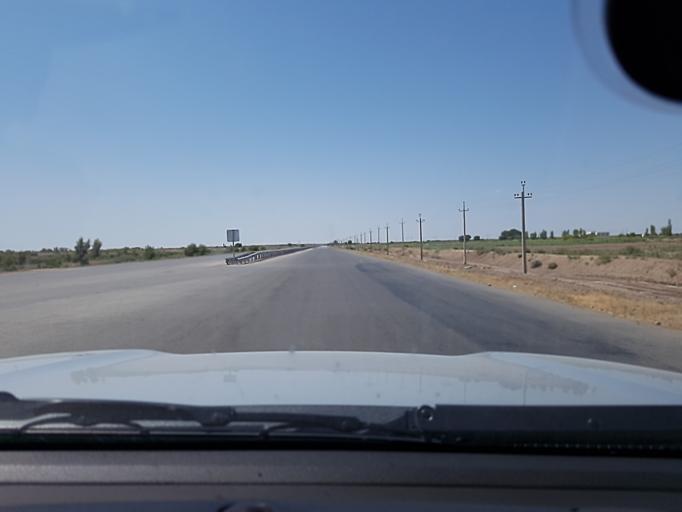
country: TM
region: Dasoguz
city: Yylanly
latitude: 41.7614
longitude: 59.4204
